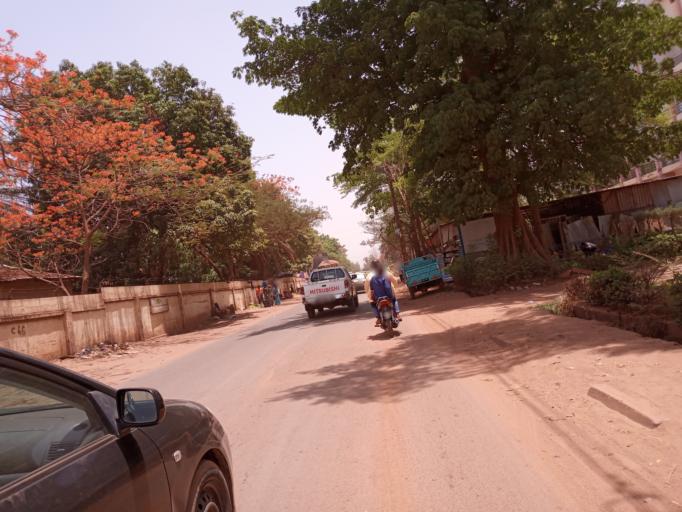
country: ML
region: Bamako
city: Bamako
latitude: 12.6489
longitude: -7.9736
